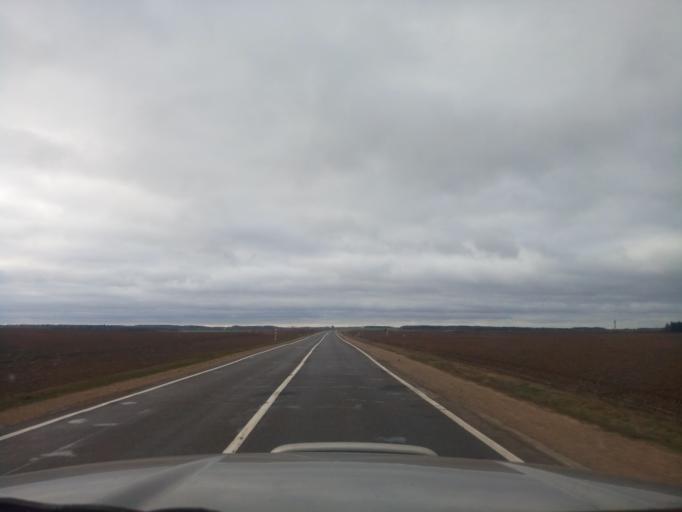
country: BY
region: Minsk
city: Kapyl'
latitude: 53.2028
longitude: 27.2193
